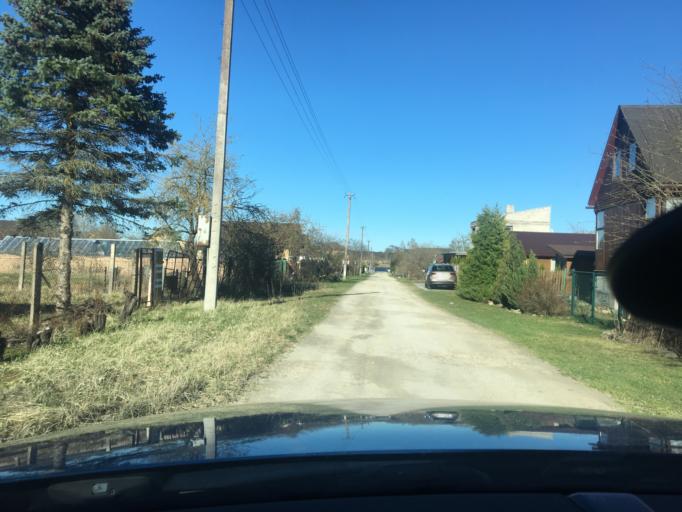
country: LV
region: Kekava
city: Kekava
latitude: 56.8546
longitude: 24.2566
